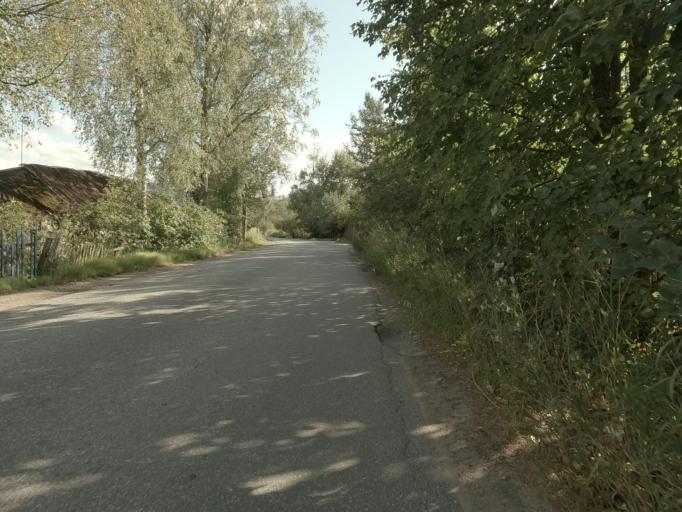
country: RU
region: Leningrad
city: Ul'yanovka
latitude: 59.6289
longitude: 30.7934
